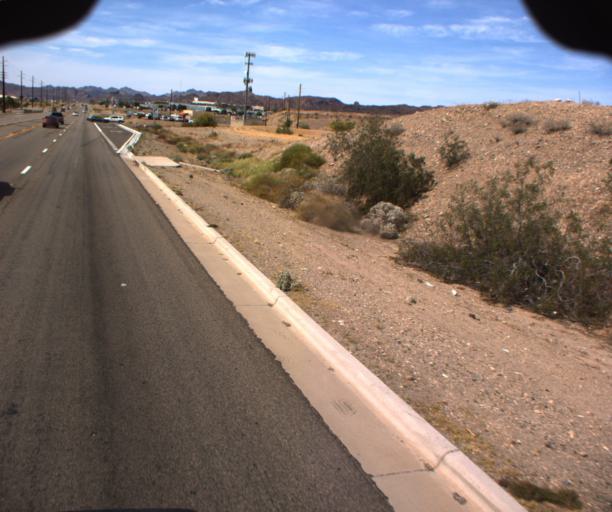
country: US
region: Arizona
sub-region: Mohave County
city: Desert Hills
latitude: 34.5368
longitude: -114.3516
